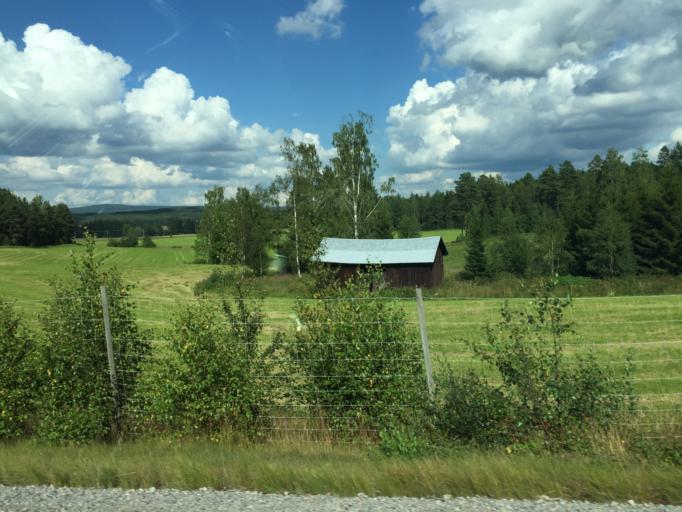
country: SE
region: Gaevleborg
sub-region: Bollnas Kommun
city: Bollnas
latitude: 61.3029
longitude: 16.4687
